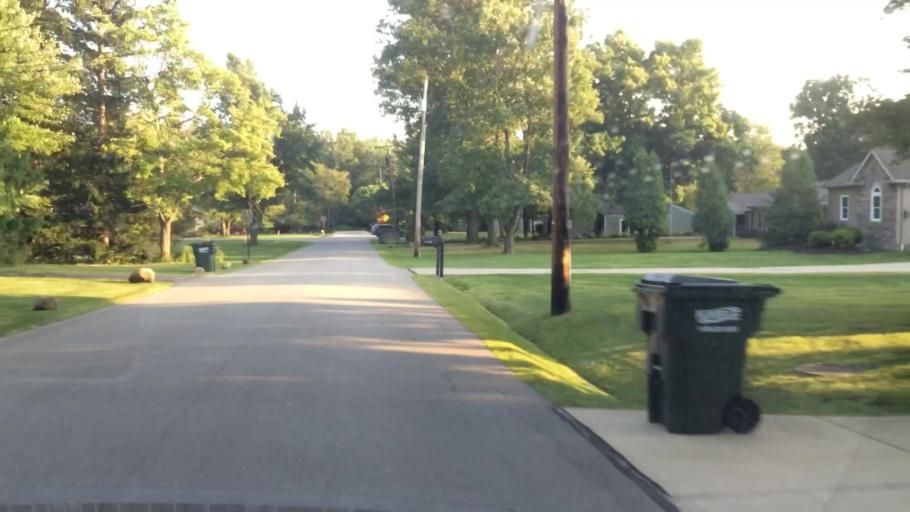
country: US
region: Ohio
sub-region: Summit County
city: Silver Lake
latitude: 41.1850
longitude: -81.4570
